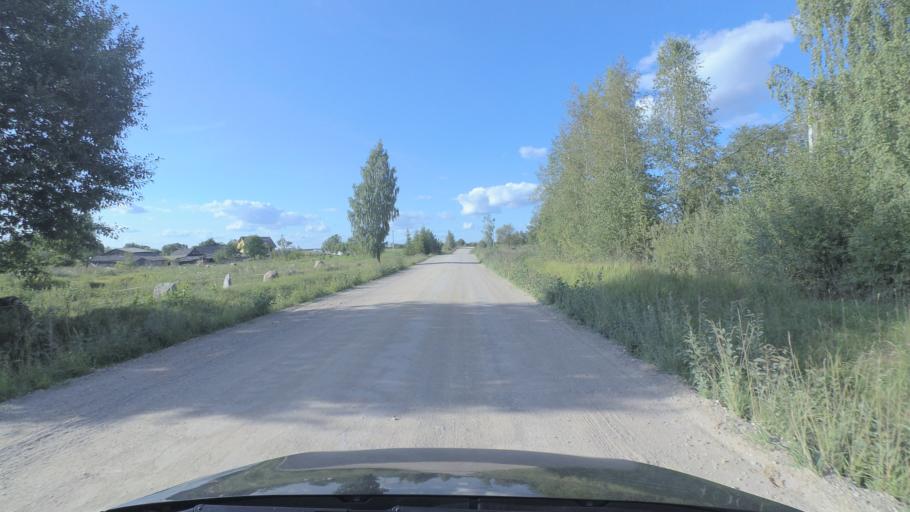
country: LT
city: Pabrade
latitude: 55.1262
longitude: 25.7053
